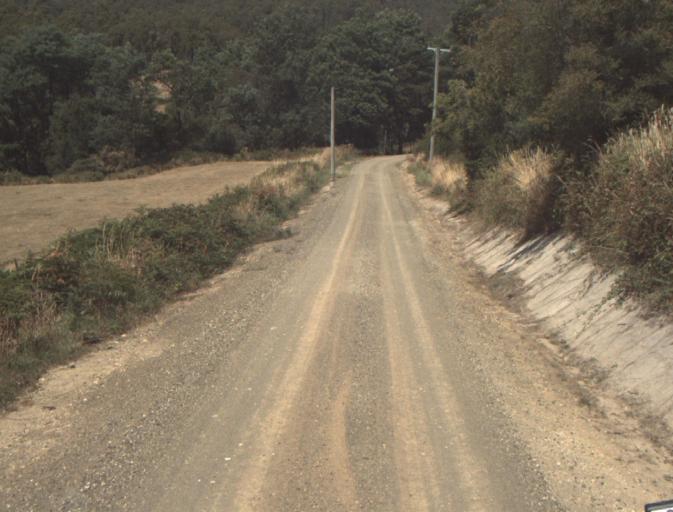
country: AU
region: Tasmania
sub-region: Launceston
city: Mayfield
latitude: -41.2678
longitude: 147.1326
